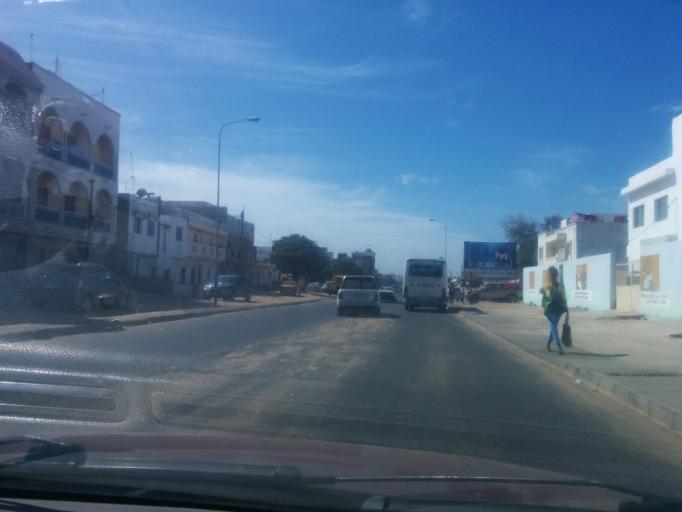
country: SN
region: Dakar
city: Pikine
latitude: 14.7820
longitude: -17.3866
